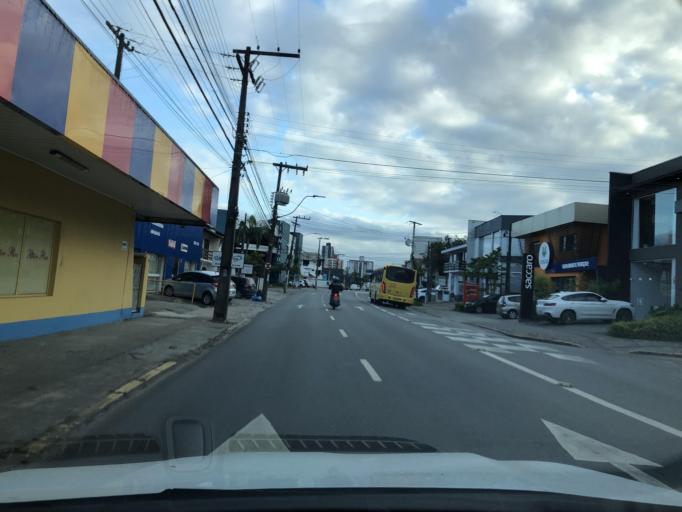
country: BR
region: Santa Catarina
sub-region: Joinville
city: Joinville
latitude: -26.2870
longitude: -48.8498
